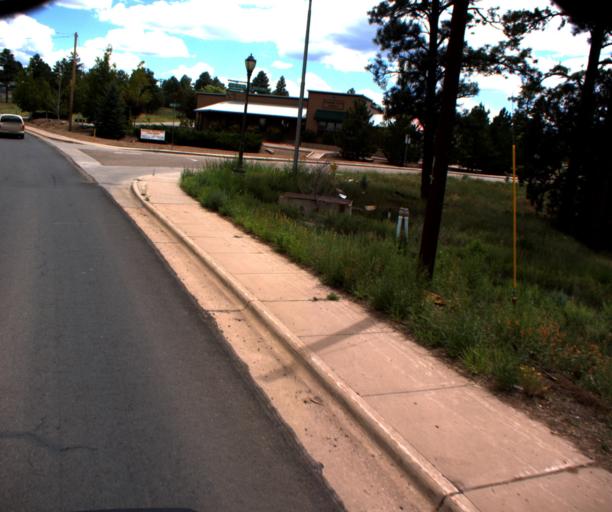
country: US
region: Arizona
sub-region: Navajo County
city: Show Low
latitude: 34.2477
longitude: -110.0279
